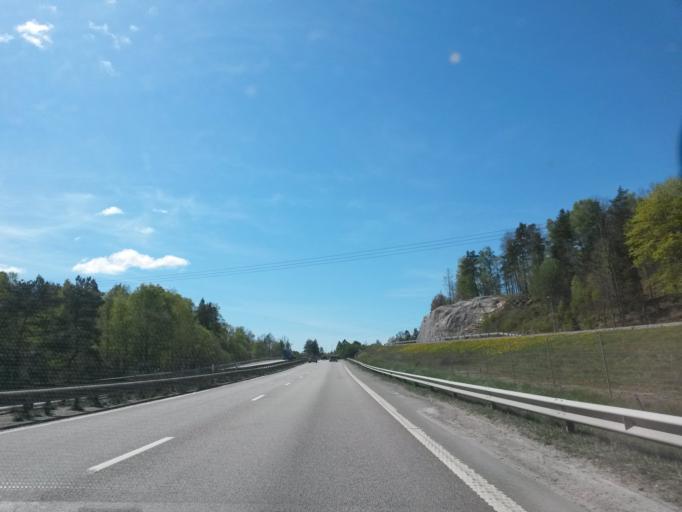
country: SE
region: Vaestra Goetaland
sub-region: Alingsas Kommun
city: Alingsas
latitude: 57.9133
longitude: 12.5116
